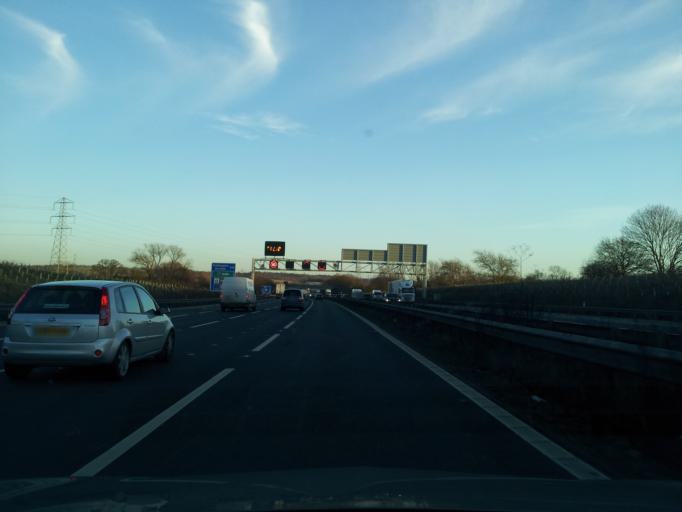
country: GB
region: England
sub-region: Central Bedfordshire
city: Toddington
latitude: 51.9568
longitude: -0.5151
